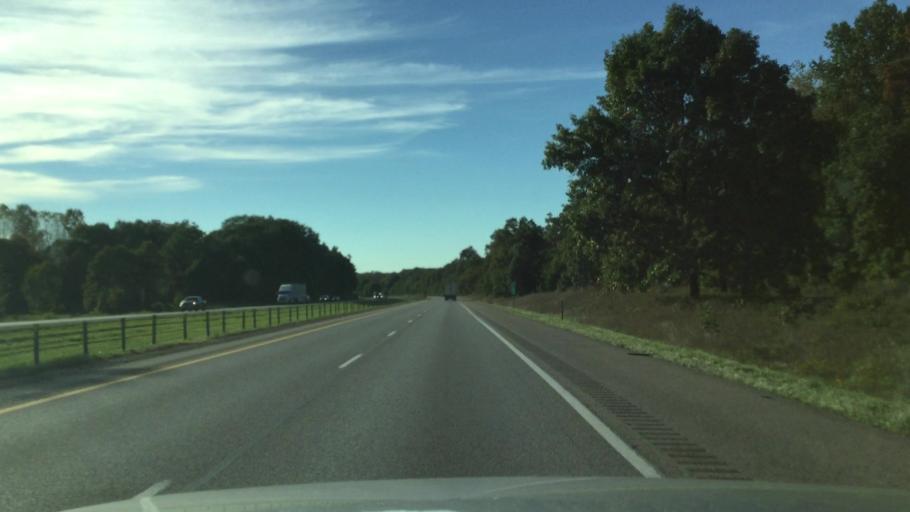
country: US
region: Michigan
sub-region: Kalamazoo County
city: Galesburg
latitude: 42.2814
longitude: -85.3413
